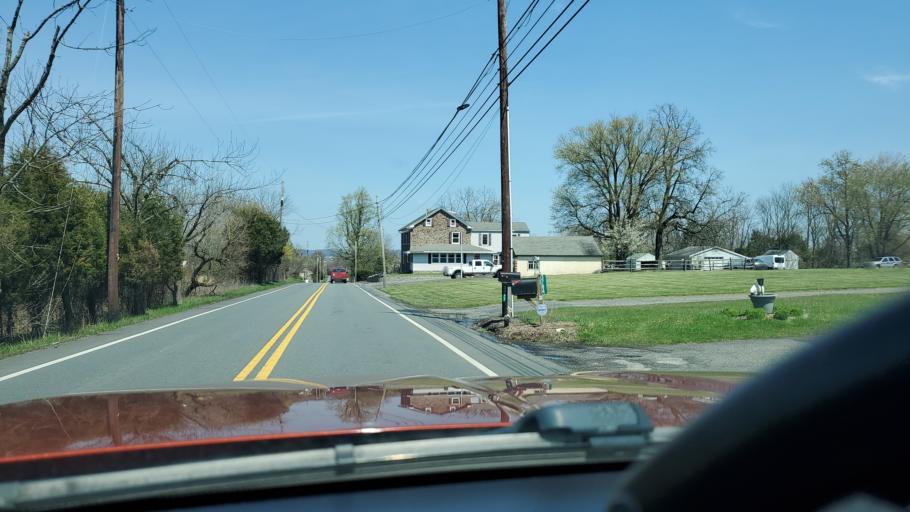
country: US
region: Pennsylvania
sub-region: Montgomery County
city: Pennsburg
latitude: 40.3611
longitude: -75.5269
